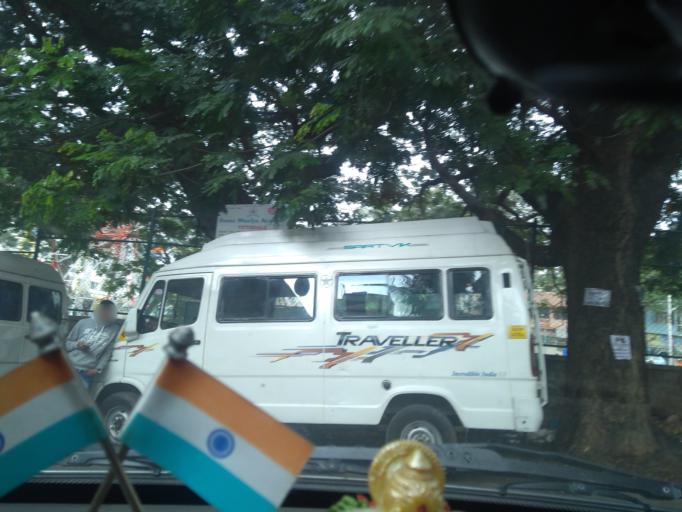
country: IN
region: Karnataka
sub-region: Bangalore Urban
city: Bangalore
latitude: 12.9810
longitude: 77.5532
